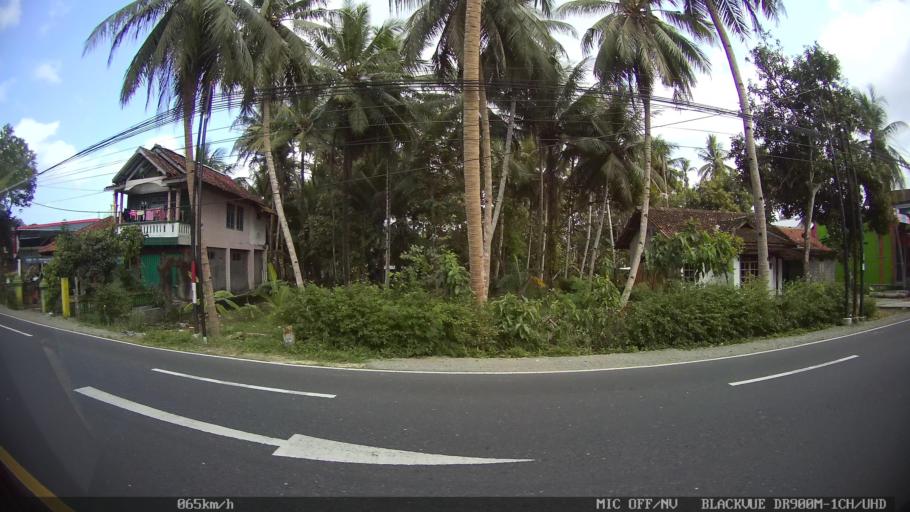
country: ID
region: Daerah Istimewa Yogyakarta
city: Srandakan
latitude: -7.8802
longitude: 110.1322
